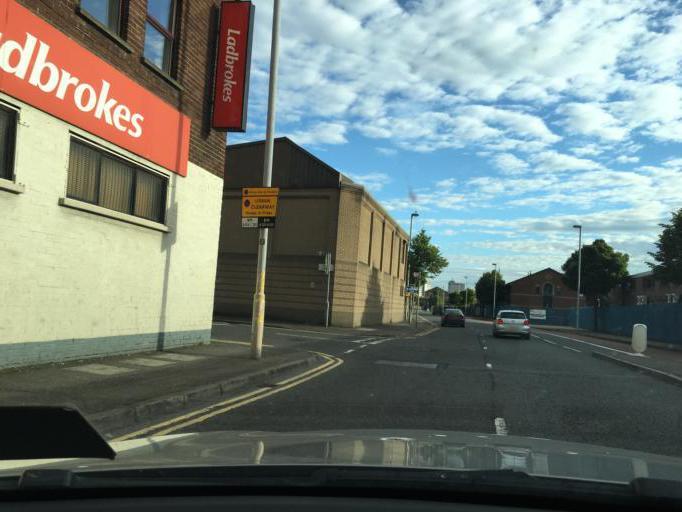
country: GB
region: Northern Ireland
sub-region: City of Belfast
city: Belfast
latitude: 54.6085
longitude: -5.9208
